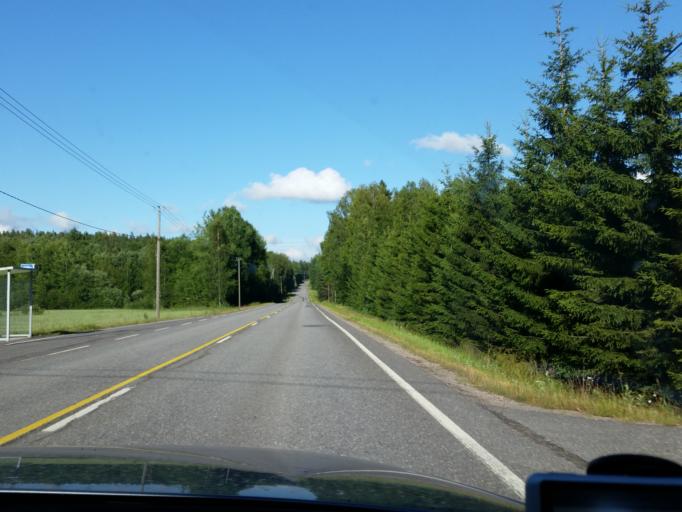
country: FI
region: Uusimaa
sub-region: Helsinki
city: Vihti
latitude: 60.3041
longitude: 24.2916
